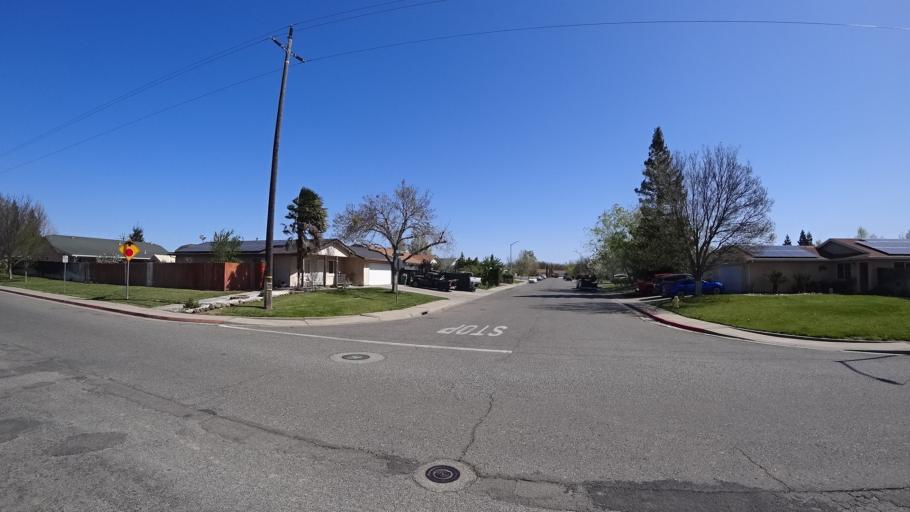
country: US
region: California
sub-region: Glenn County
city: Hamilton City
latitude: 39.7459
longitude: -122.0086
